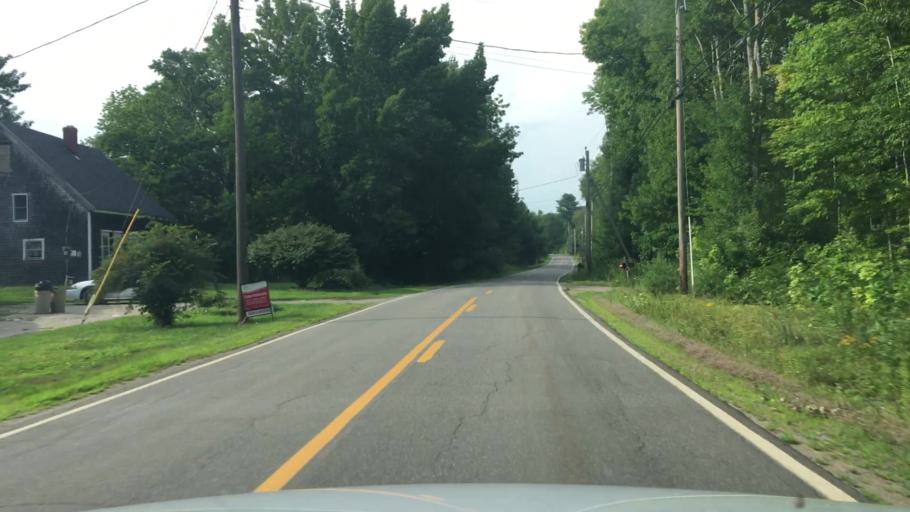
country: US
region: Maine
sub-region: Lincoln County
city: Waldoboro
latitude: 44.1658
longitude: -69.3778
